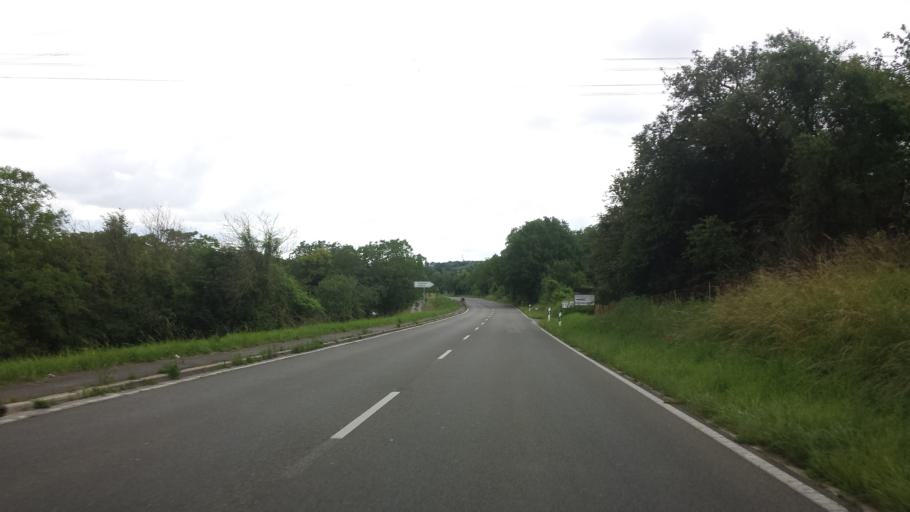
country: DE
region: Baden-Wuerttemberg
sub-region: Karlsruhe Region
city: Nussloch
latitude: 49.3355
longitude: 8.6948
